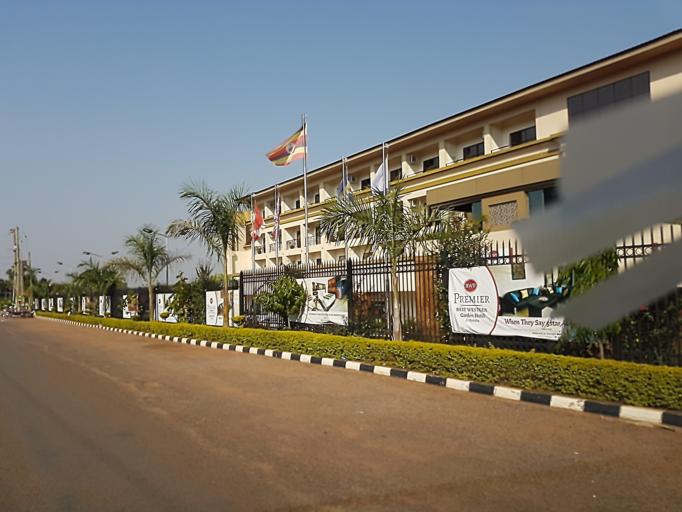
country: UG
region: Central Region
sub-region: Wakiso District
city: Entebbe
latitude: 0.0660
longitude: 32.4756
